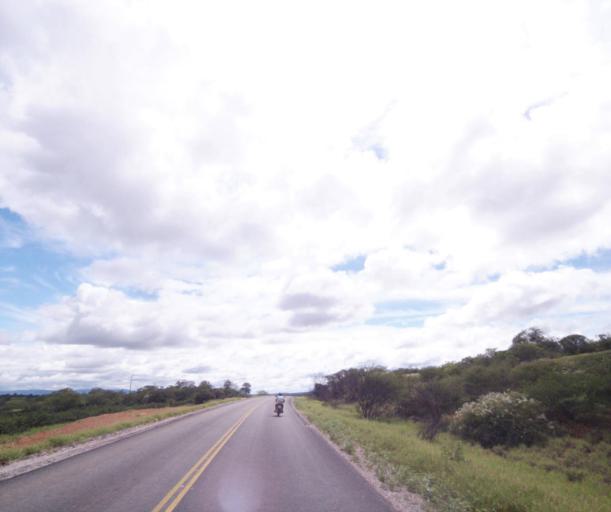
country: BR
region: Bahia
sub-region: Brumado
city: Brumado
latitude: -14.1515
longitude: -41.5084
